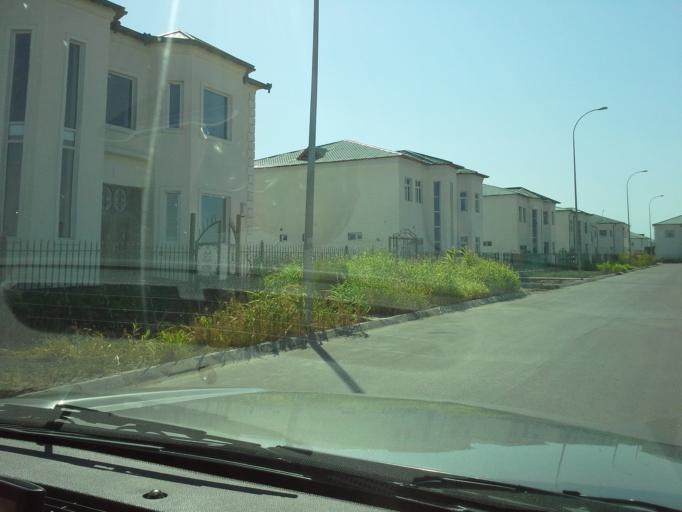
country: TM
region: Dasoguz
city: Dasoguz
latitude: 41.8105
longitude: 59.9558
